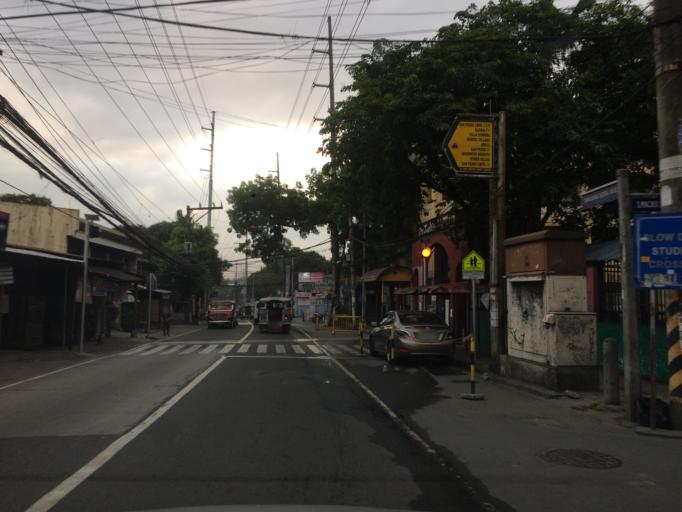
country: PH
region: Calabarzon
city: Bagong Pagasa
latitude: 14.6746
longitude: 121.0468
